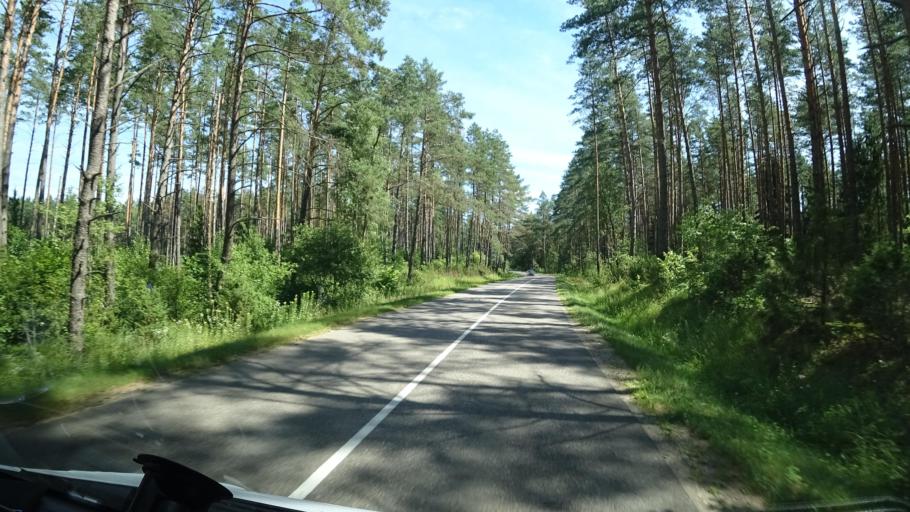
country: LT
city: Trakai
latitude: 54.5288
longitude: 24.9709
